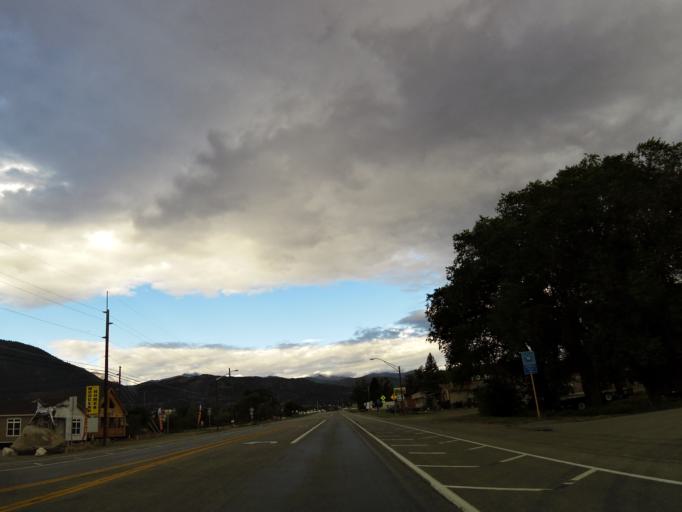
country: US
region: Colorado
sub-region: Chaffee County
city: Salida
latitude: 38.5156
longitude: -106.0706
